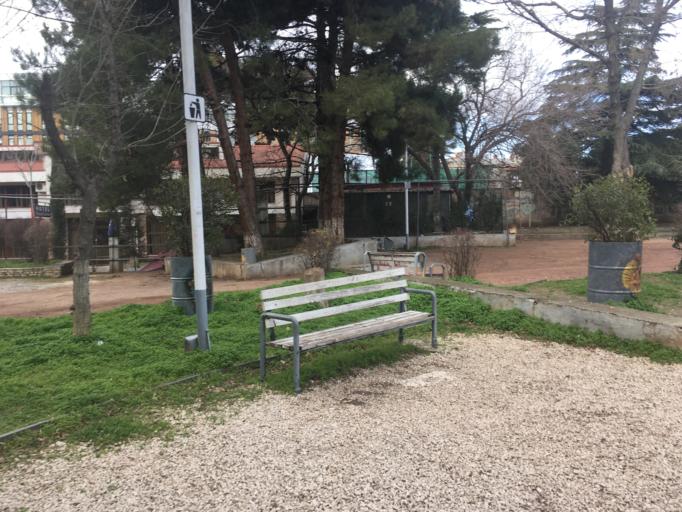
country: GE
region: T'bilisi
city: Tbilisi
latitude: 41.7088
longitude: 44.7997
